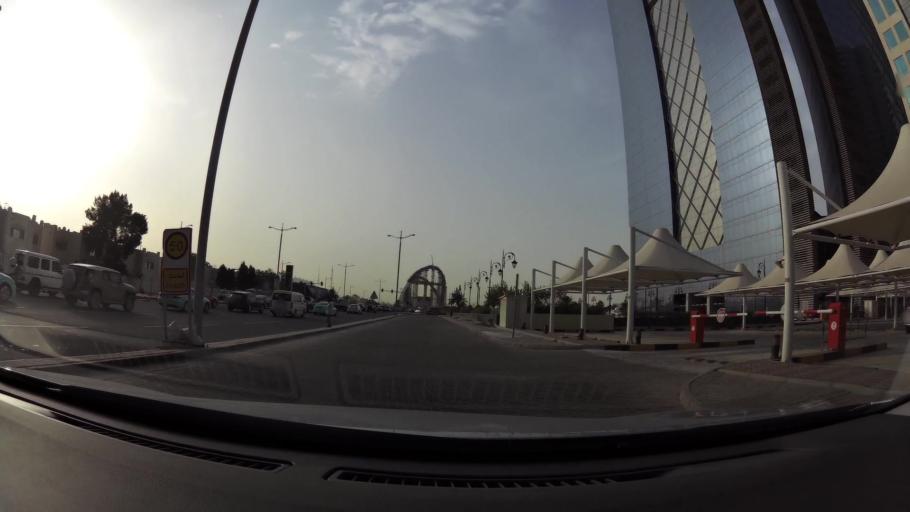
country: QA
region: Baladiyat ad Dawhah
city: Doha
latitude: 25.3293
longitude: 51.5246
